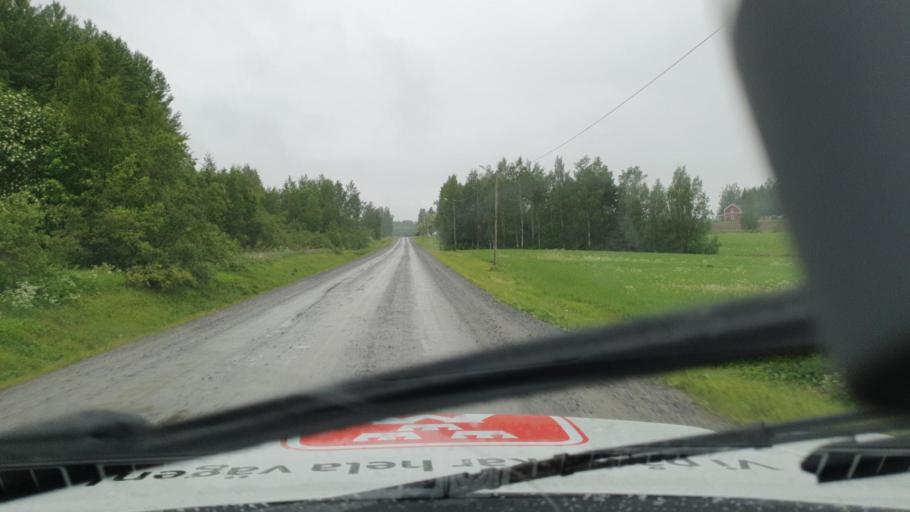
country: SE
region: Vaesterbotten
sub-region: Bjurholms Kommun
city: Bjurholm
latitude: 63.8677
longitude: 19.4611
